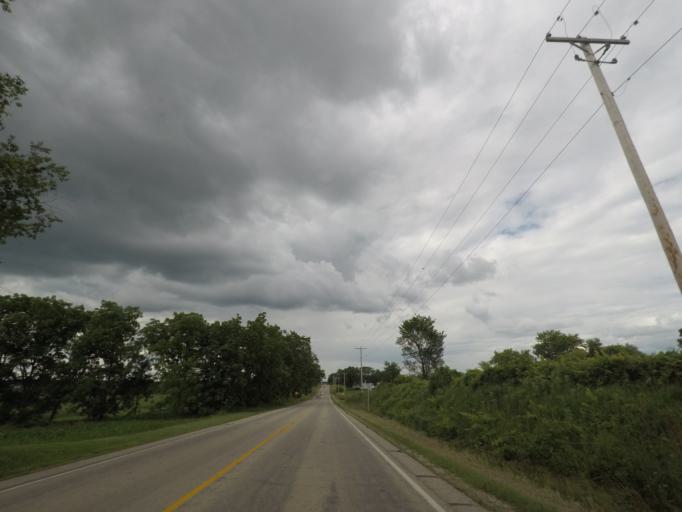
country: US
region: Wisconsin
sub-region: Green County
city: Brooklyn
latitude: 42.8385
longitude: -89.4126
